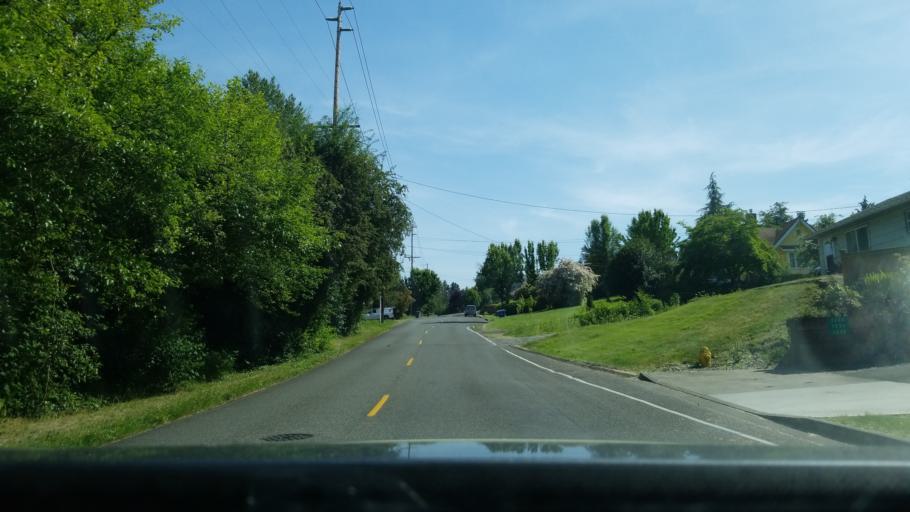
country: US
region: Washington
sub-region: Pierce County
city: Puyallup
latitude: 47.1793
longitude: -122.3054
